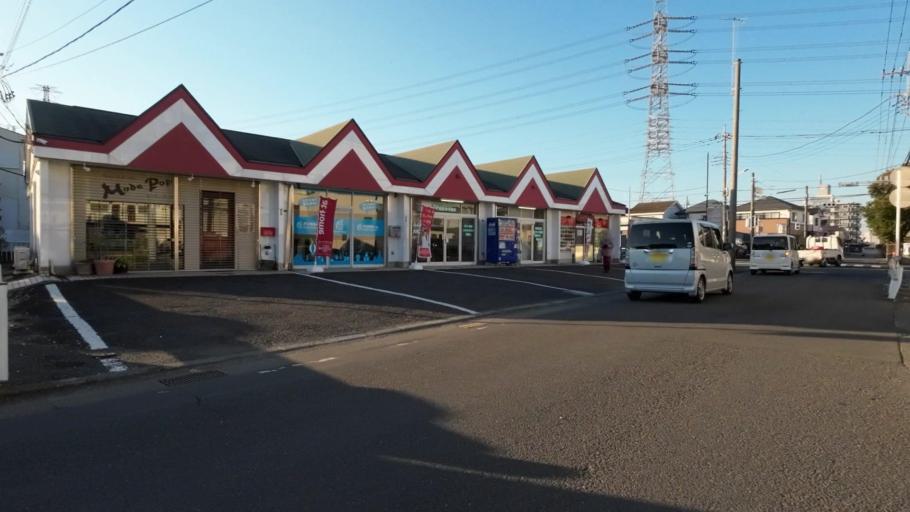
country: JP
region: Kanagawa
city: Atsugi
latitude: 35.4077
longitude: 139.3787
